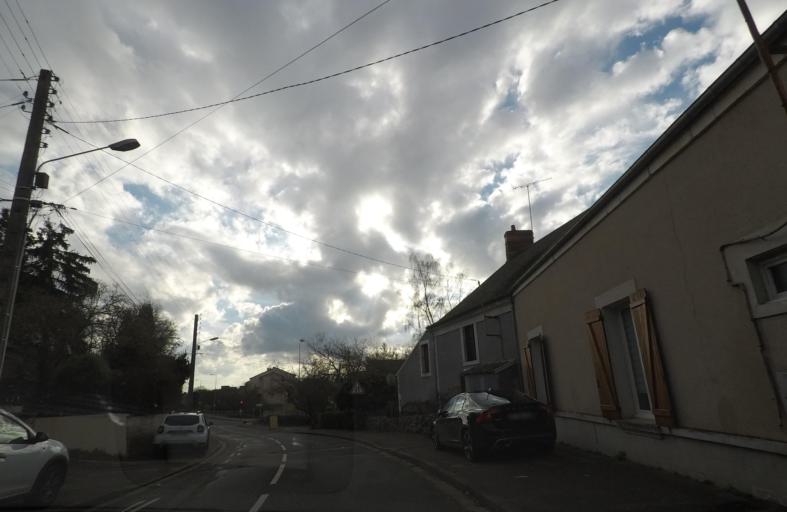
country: FR
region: Centre
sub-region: Departement du Cher
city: Bourges
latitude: 47.0614
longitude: 2.4009
